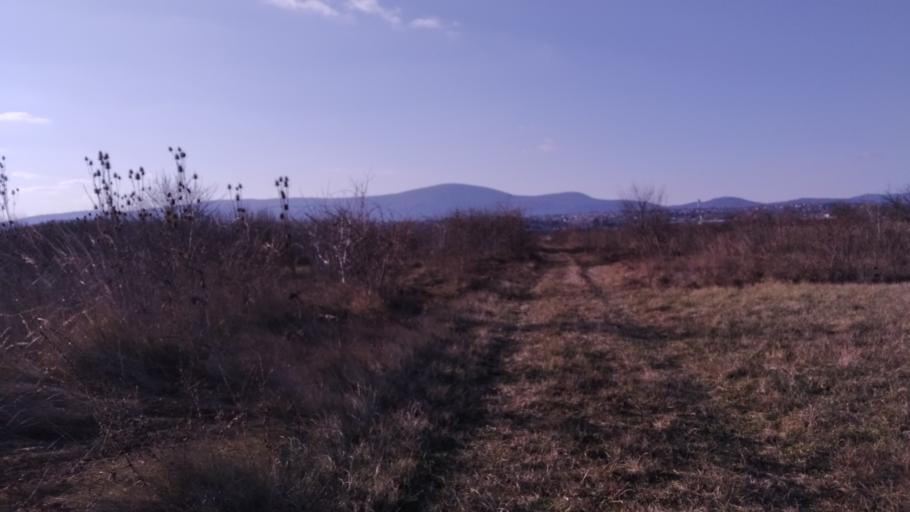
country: HU
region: Pest
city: Budakalasz
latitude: 47.6352
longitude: 19.0562
